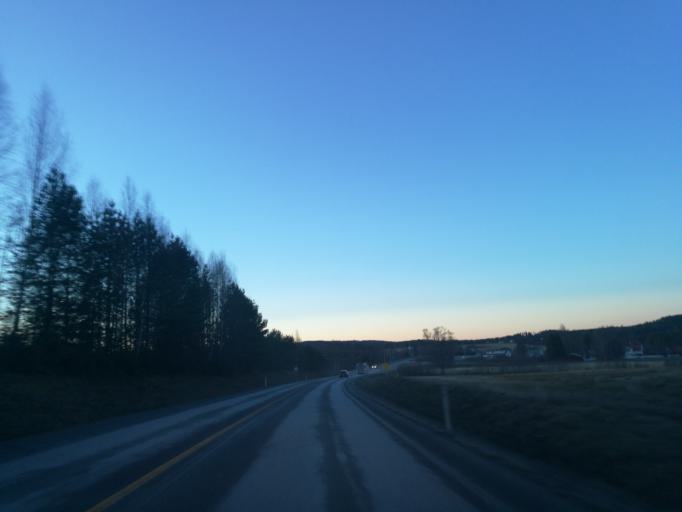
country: NO
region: Hedmark
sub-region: Eidskog
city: Skotterud
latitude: 59.9779
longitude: 12.1211
